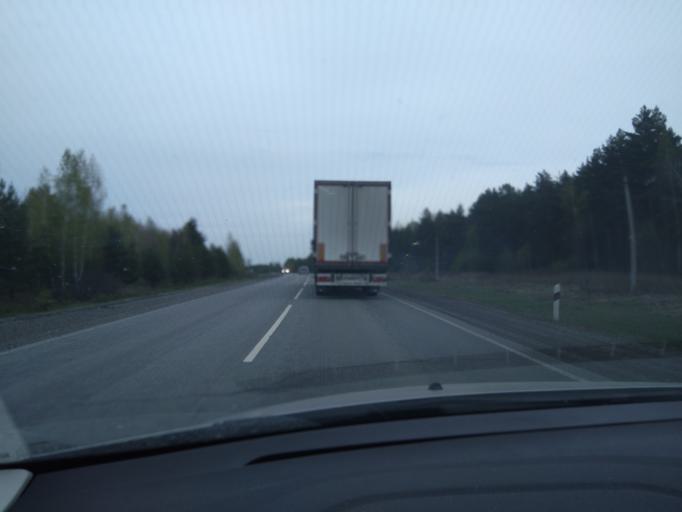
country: RU
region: Sverdlovsk
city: Pyshma
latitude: 57.0462
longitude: 63.4769
